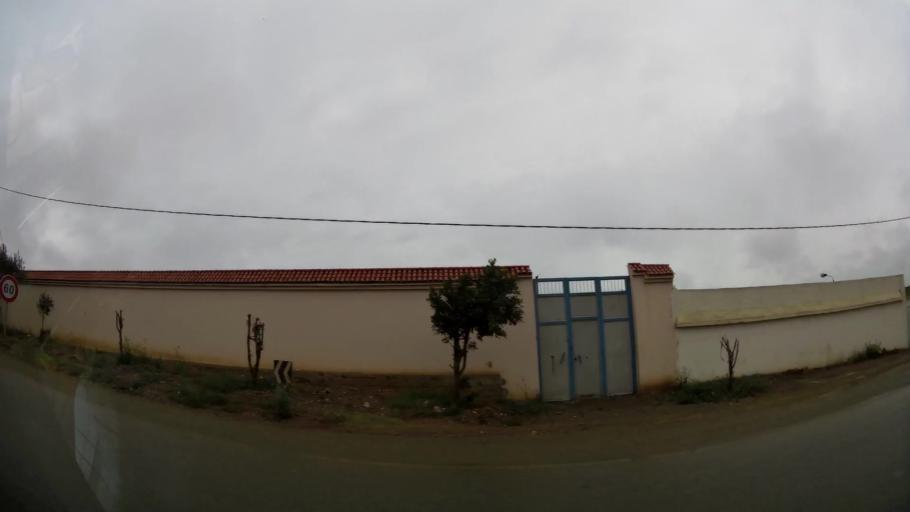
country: MA
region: Taza-Al Hoceima-Taounate
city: Imzourene
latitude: 35.1932
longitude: -3.8908
